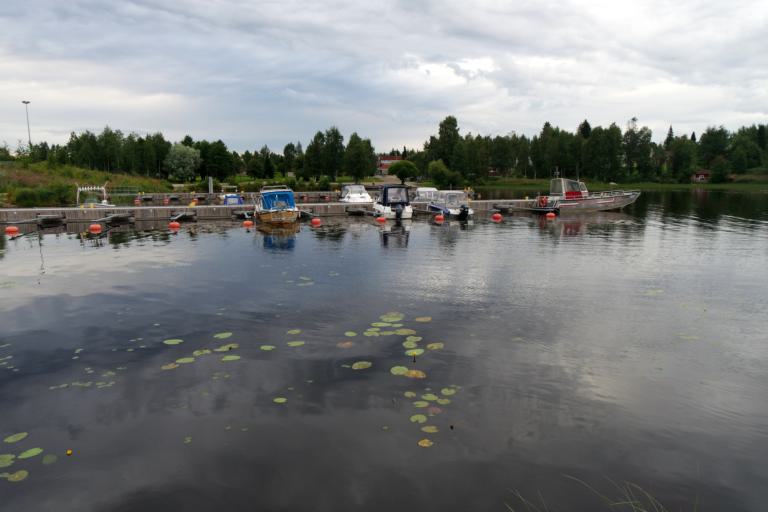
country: FI
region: Northern Ostrobothnia
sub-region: Nivala-Haapajaervi
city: Pyhaesalmi
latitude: 63.6809
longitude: 25.9846
